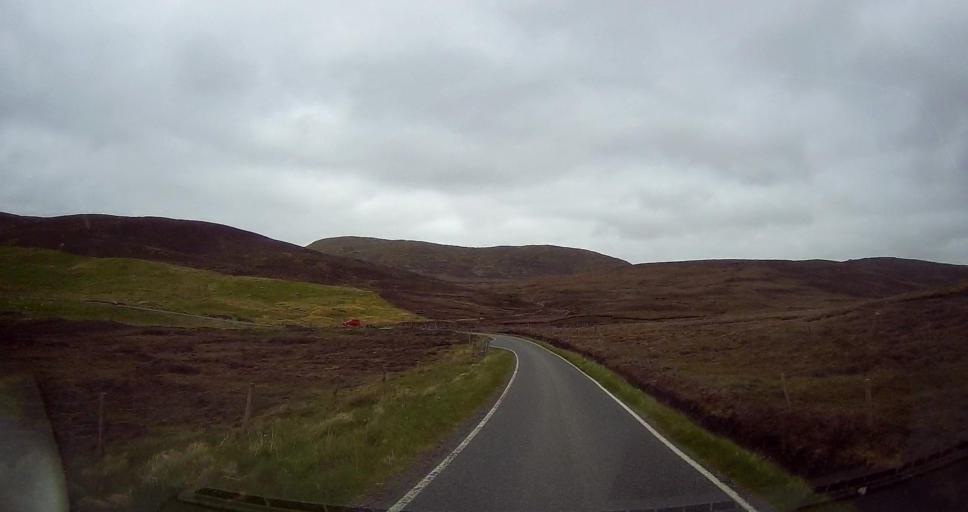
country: GB
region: Scotland
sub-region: Shetland Islands
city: Lerwick
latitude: 60.3007
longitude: -1.3422
